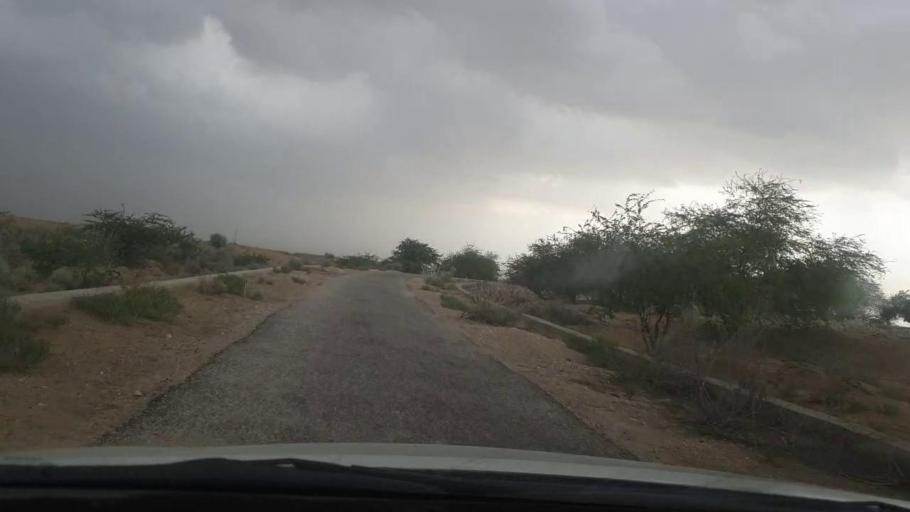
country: PK
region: Sindh
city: Khairpur
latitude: 27.4400
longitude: 68.9825
